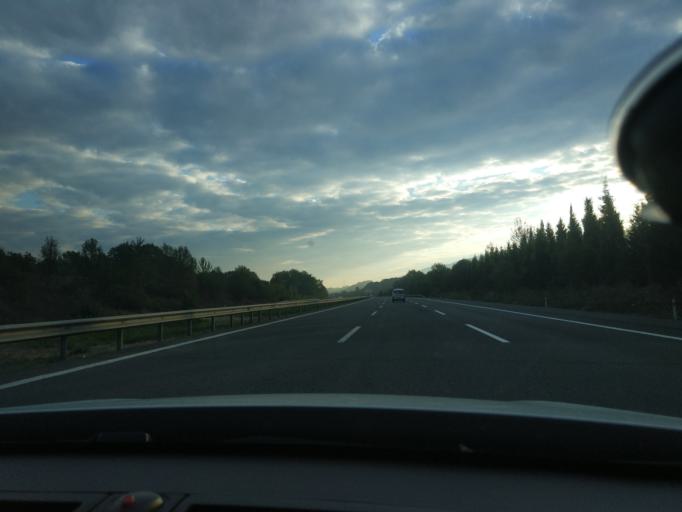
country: TR
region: Sakarya
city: Hendek
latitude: 40.7553
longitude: 30.7386
